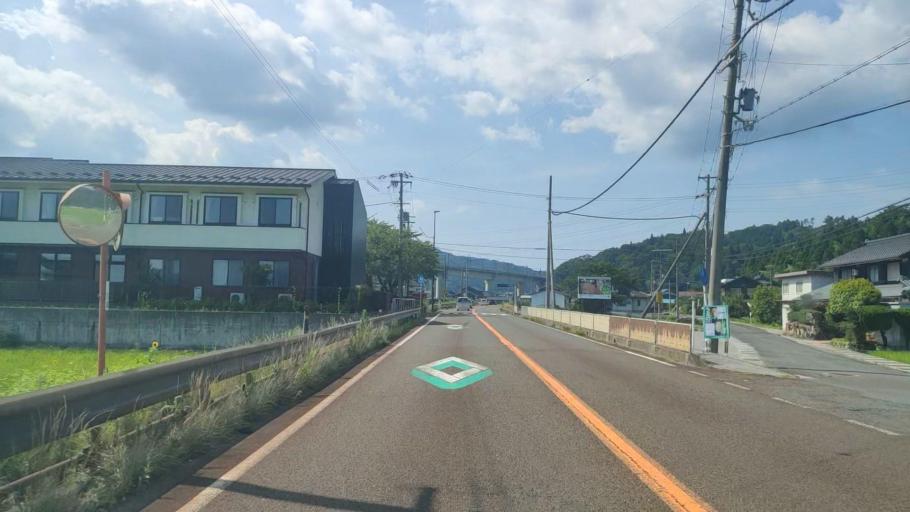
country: JP
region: Fukui
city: Tsuruga
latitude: 35.5274
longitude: 136.1580
